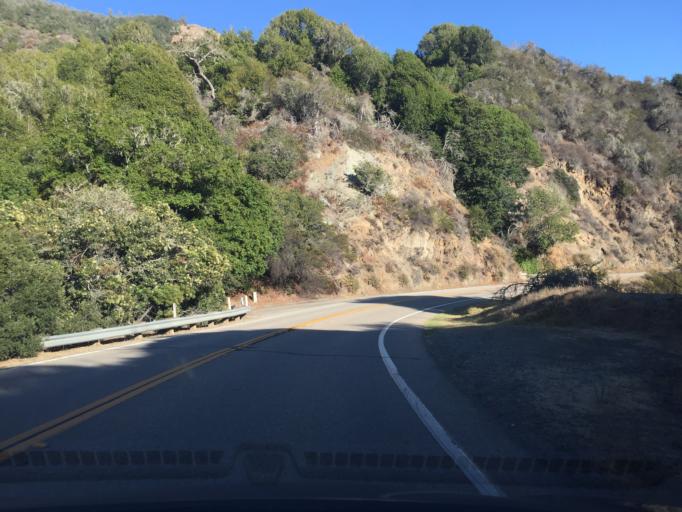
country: US
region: California
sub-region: San Luis Obispo County
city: Cambria
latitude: 35.8218
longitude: -121.3750
